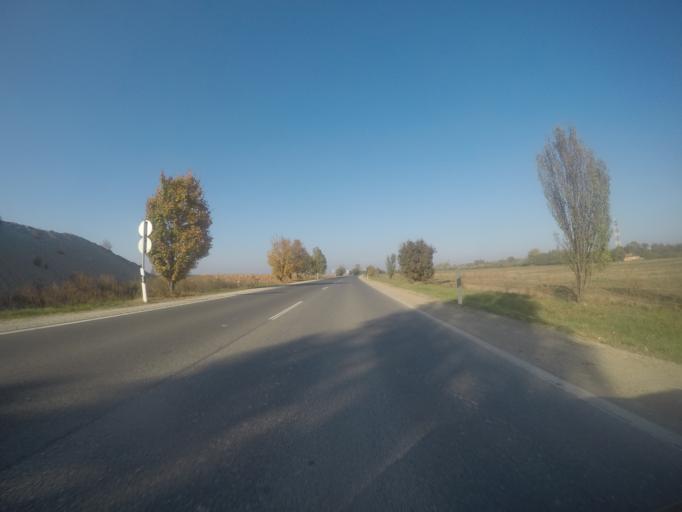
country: HU
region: Fejer
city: Ercsi
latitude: 47.2868
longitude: 18.8737
